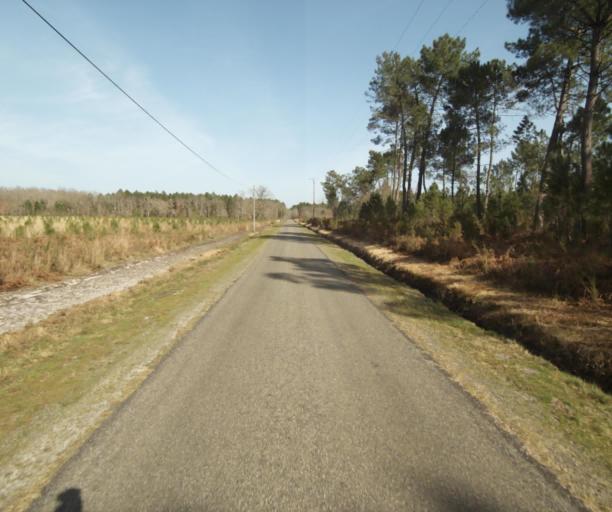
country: FR
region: Aquitaine
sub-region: Departement des Landes
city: Roquefort
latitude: 44.1449
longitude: -0.2384
